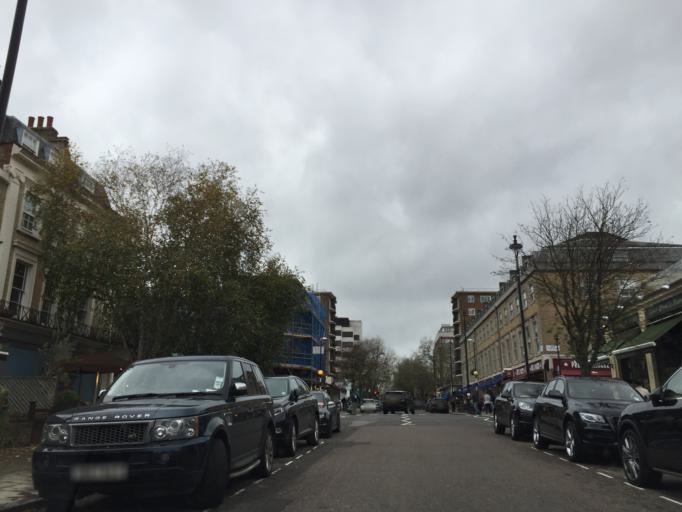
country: GB
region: England
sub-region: Greater London
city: Belsize Park
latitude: 51.5343
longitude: -0.1708
